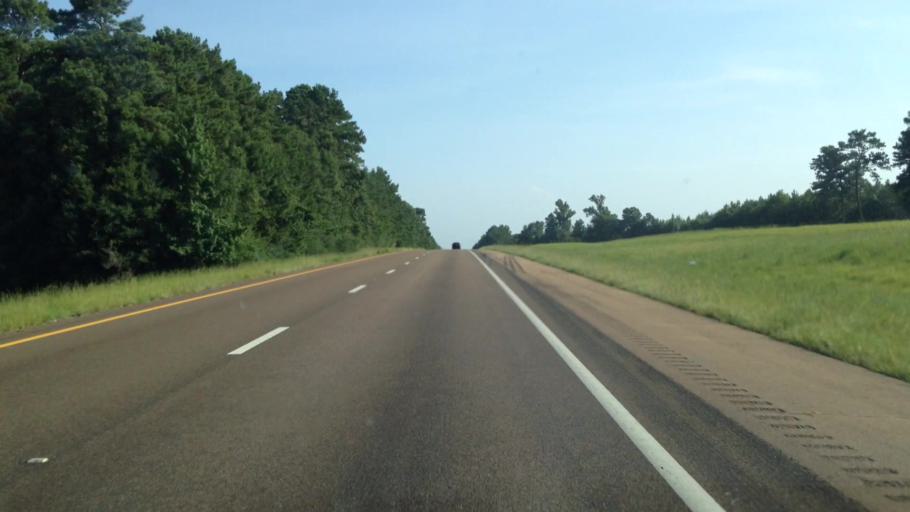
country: US
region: Mississippi
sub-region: Pike County
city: Summit
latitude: 31.3669
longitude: -90.4791
